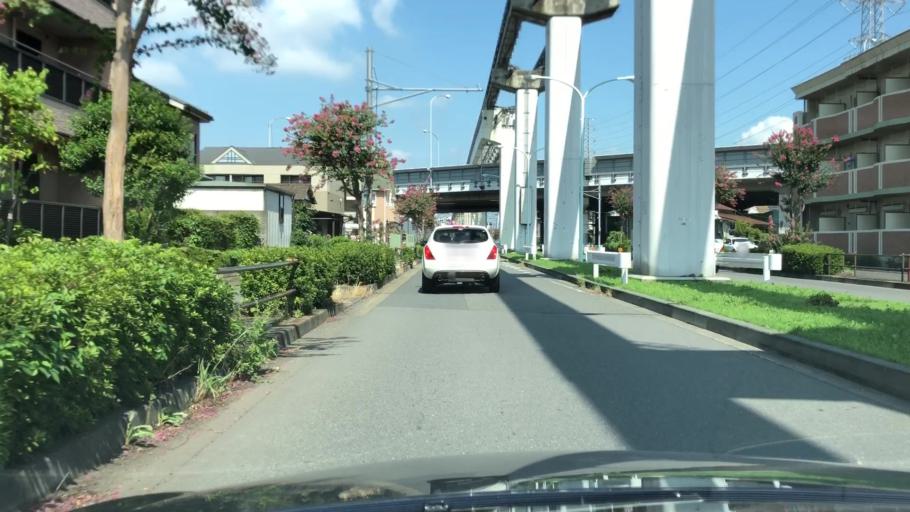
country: JP
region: Tokyo
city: Hino
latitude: 35.6746
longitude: 139.4151
